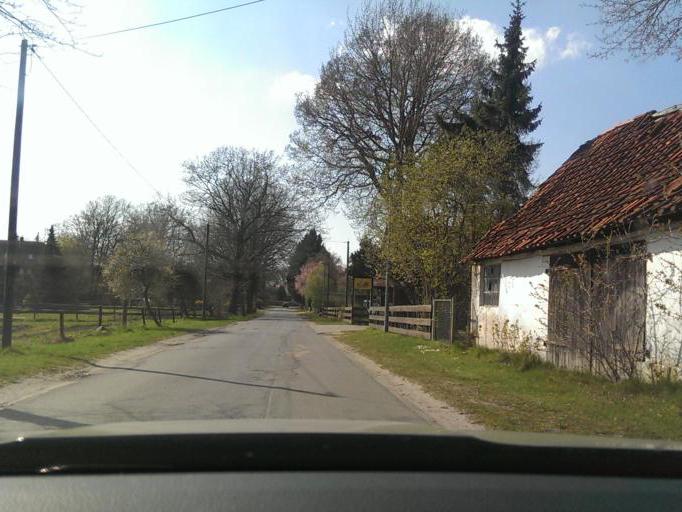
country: DE
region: Lower Saxony
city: Elze
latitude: 52.5635
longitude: 9.7322
